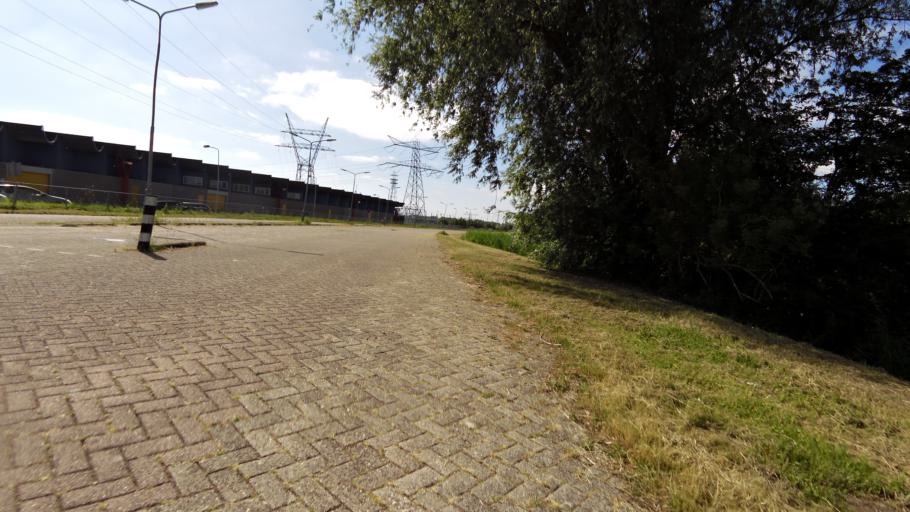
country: NL
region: North Holland
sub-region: Gemeente Amsterdam
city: Driemond
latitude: 52.3350
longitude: 5.0241
